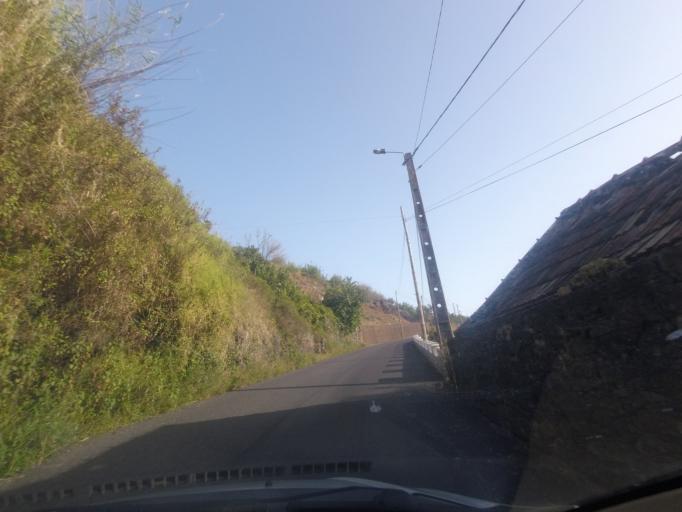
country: PT
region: Madeira
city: Ponta do Sol
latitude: 32.6837
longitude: -17.0728
